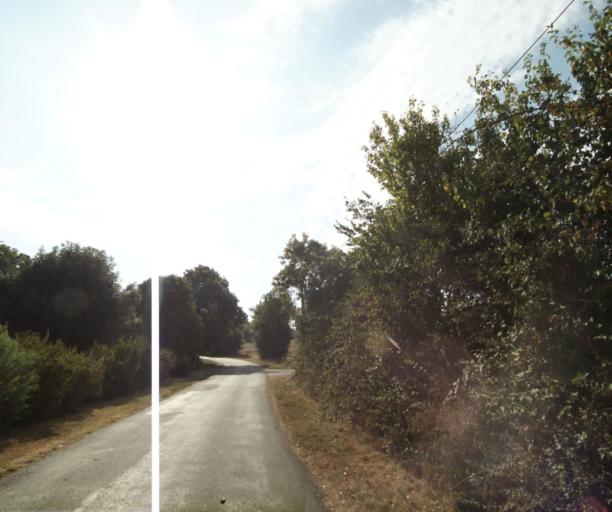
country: FR
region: Poitou-Charentes
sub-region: Departement de la Charente-Maritime
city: Tonnay-Charente
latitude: 45.9655
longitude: -0.8632
